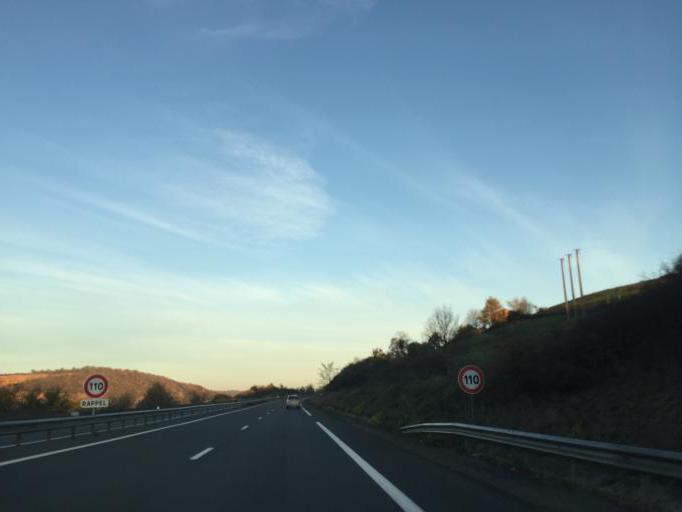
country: FR
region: Rhone-Alpes
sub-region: Departement de la Loire
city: Commelle-Vernay
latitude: 45.9772
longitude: 4.1243
